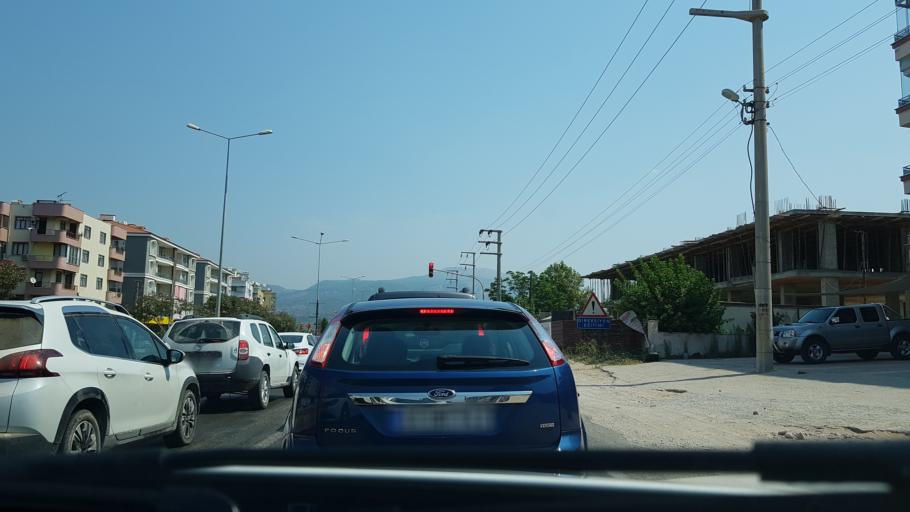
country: TR
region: Mugla
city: Milas
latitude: 37.3102
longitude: 27.7903
